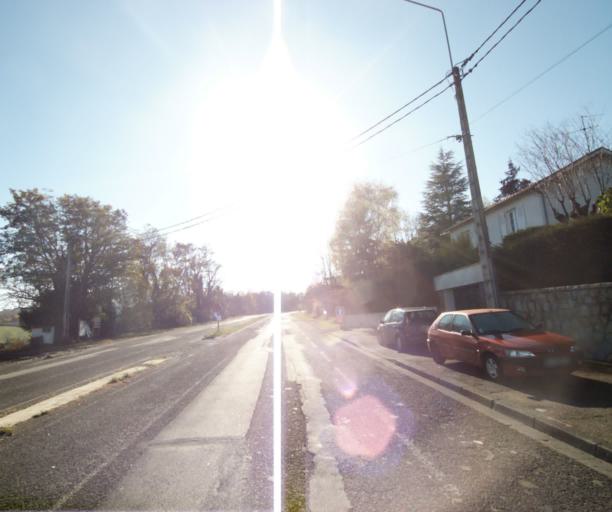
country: FR
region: Auvergne
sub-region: Departement du Puy-de-Dome
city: Ceyrat
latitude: 45.7443
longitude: 3.0700
